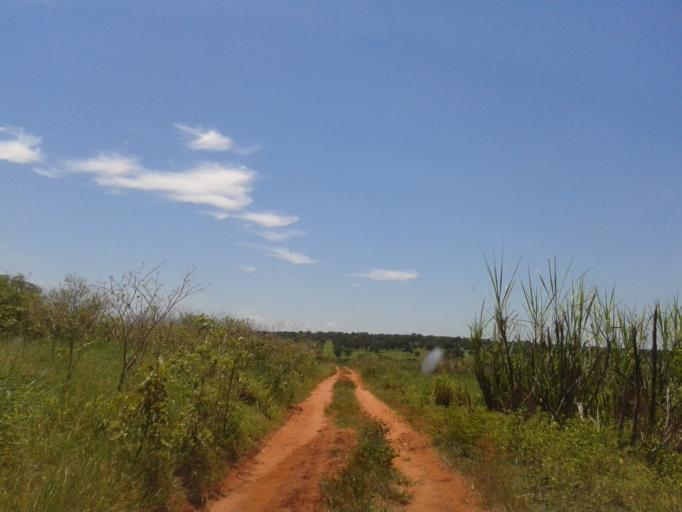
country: BR
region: Minas Gerais
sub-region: Santa Vitoria
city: Santa Vitoria
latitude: -19.1637
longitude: -50.5422
